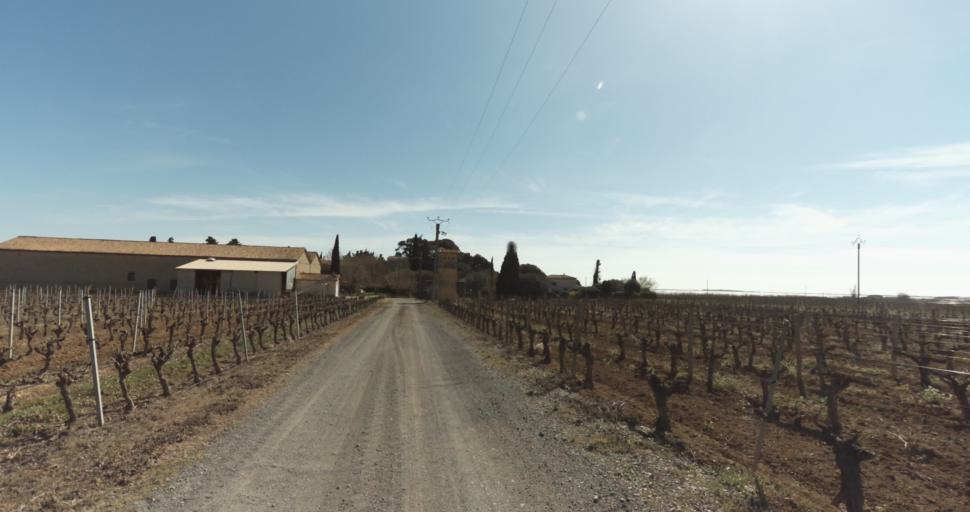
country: FR
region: Languedoc-Roussillon
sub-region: Departement de l'Herault
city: Marseillan
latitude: 43.3759
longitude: 3.5398
